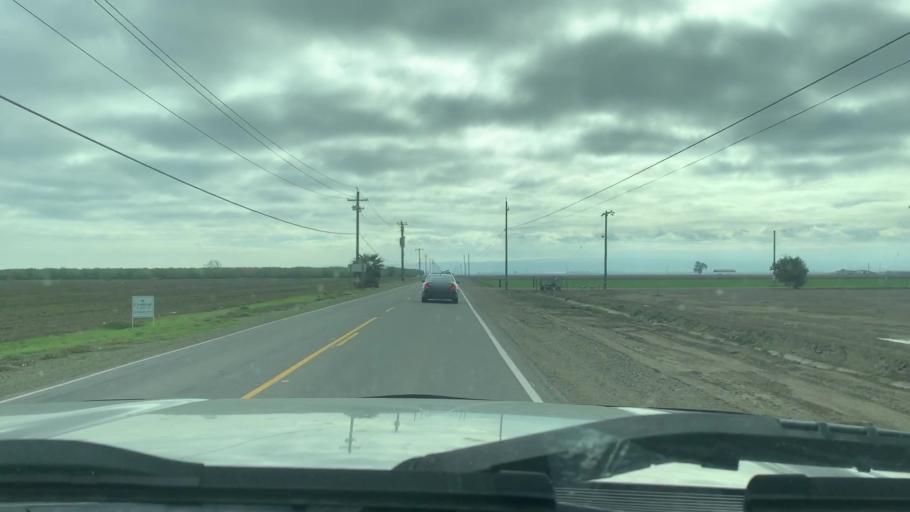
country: US
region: California
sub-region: Merced County
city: Los Banos
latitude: 37.0267
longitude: -120.8362
